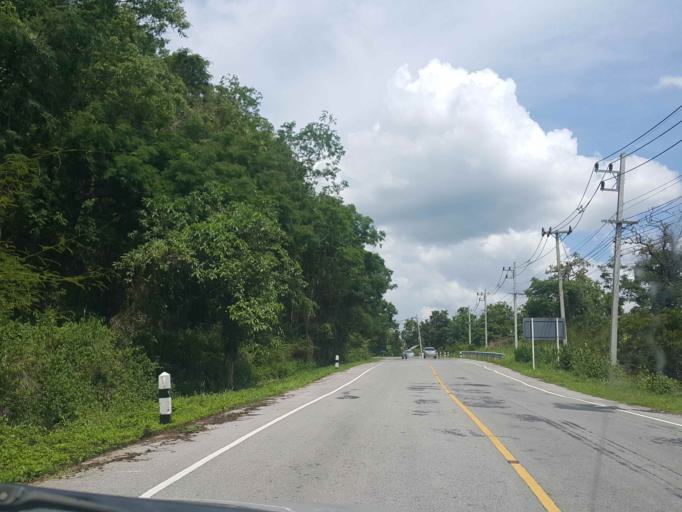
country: TH
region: Nan
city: Ban Luang
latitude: 18.8744
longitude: 100.4885
